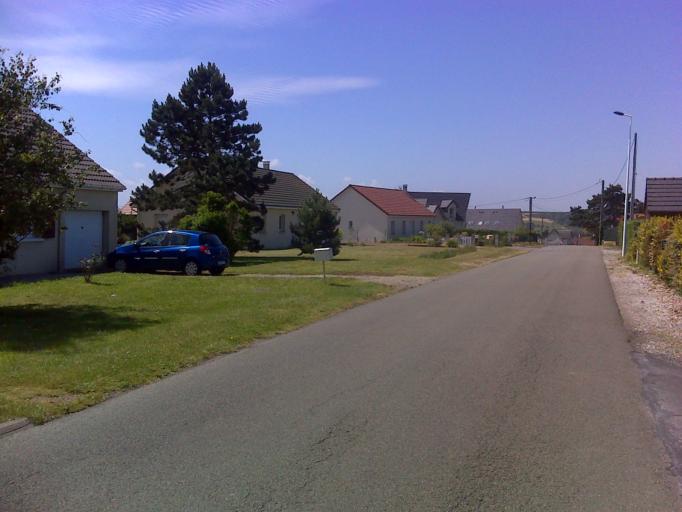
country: FR
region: Haute-Normandie
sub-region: Departement de la Seine-Maritime
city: Criel-sur-Mer
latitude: 50.0363
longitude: 1.3254
